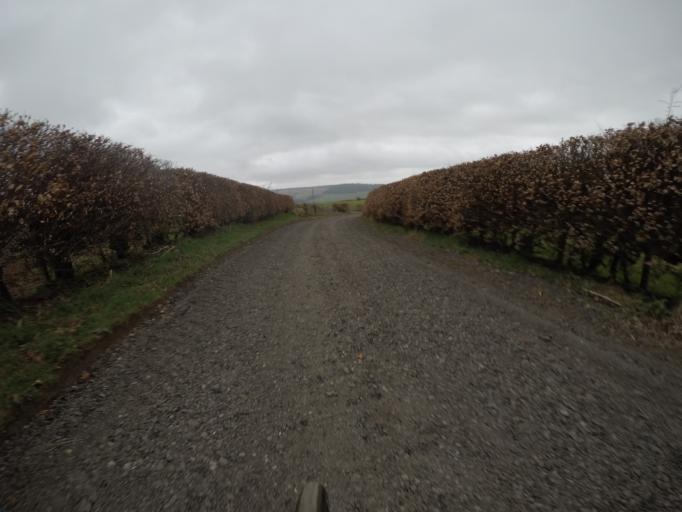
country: GB
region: Scotland
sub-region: East Ayrshire
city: Newmilns
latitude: 55.6229
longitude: -4.3428
